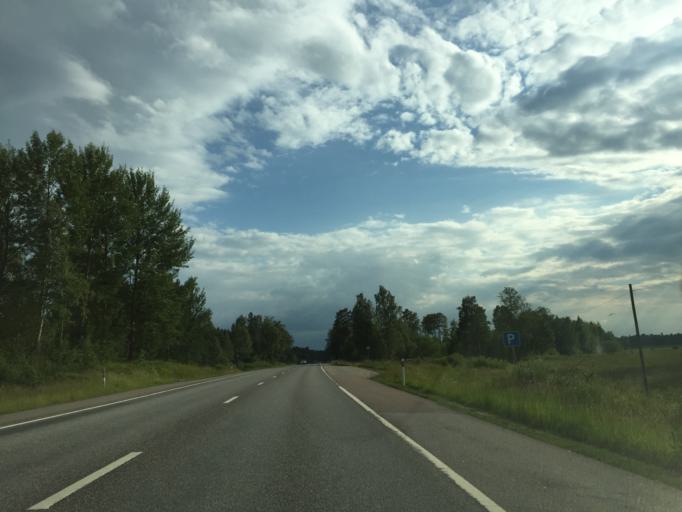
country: SE
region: OErebro
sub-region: Lindesbergs Kommun
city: Fellingsbro
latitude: 59.3623
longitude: 15.6924
